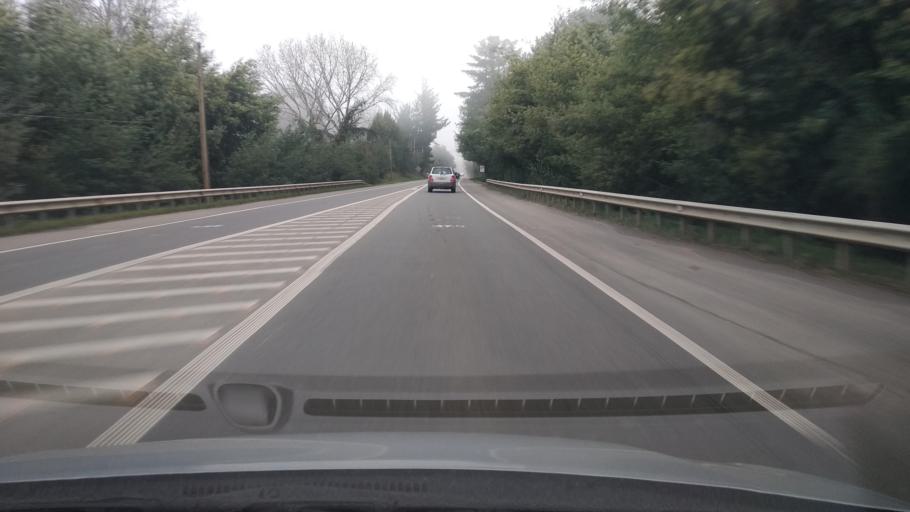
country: CL
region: Los Lagos
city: Las Animas
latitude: -39.7336
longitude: -73.2121
